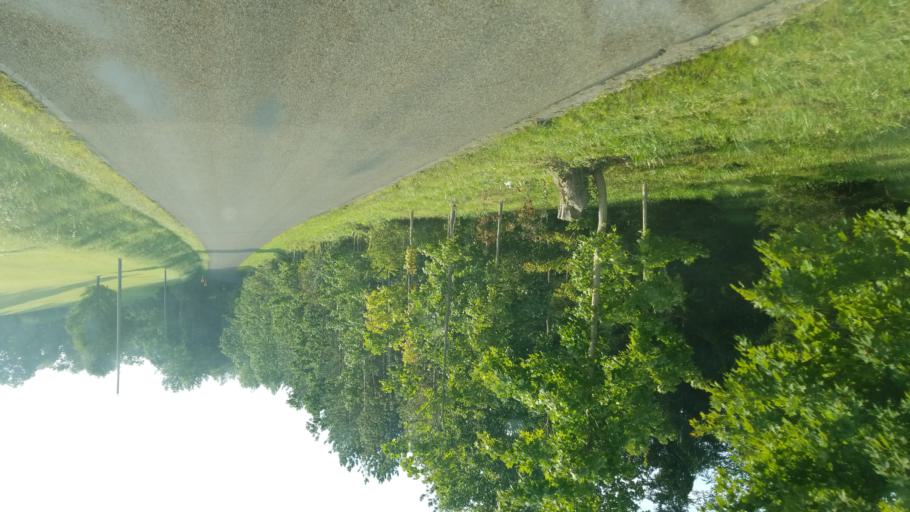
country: US
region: Ohio
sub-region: Sandusky County
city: Bellville
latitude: 40.6471
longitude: -82.4886
